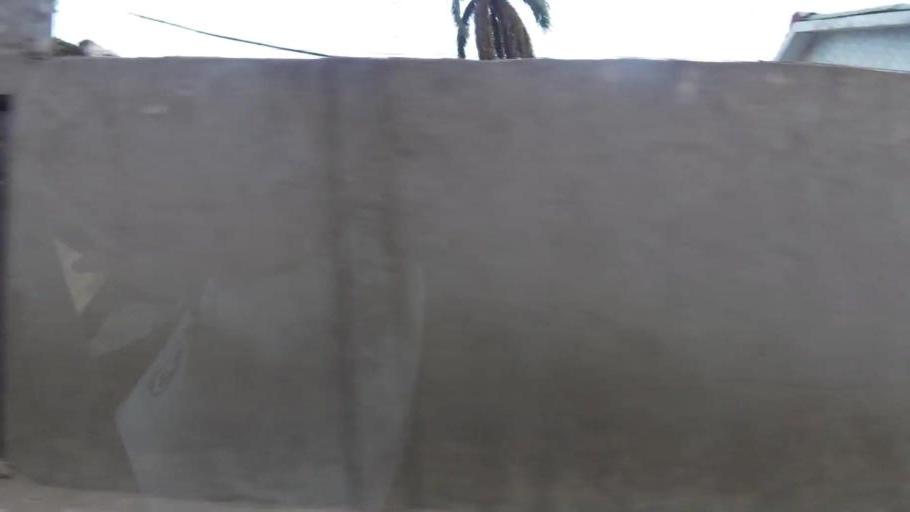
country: CO
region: Bolivar
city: Cartagena
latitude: 10.4097
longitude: -75.5505
